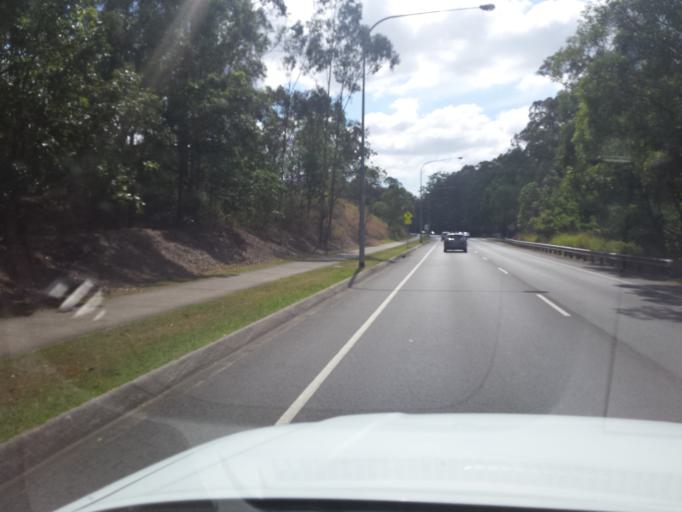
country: AU
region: Queensland
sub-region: Brisbane
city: Everton Park
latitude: -27.3828
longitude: 152.9678
